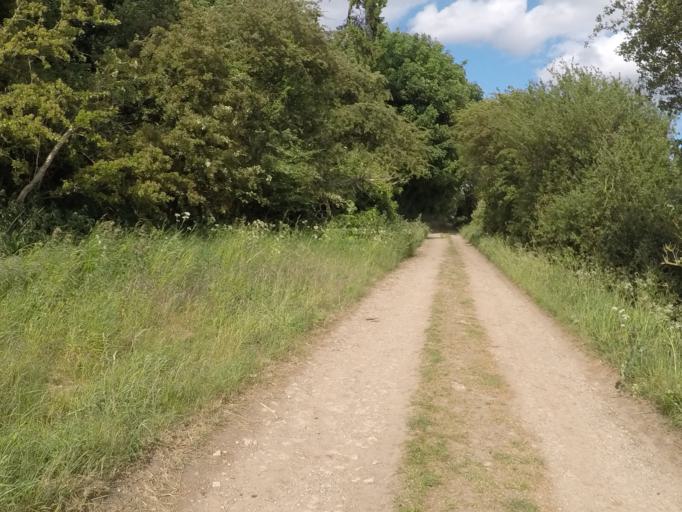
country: GB
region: England
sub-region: Oxfordshire
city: Witney
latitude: 51.8251
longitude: -1.5106
